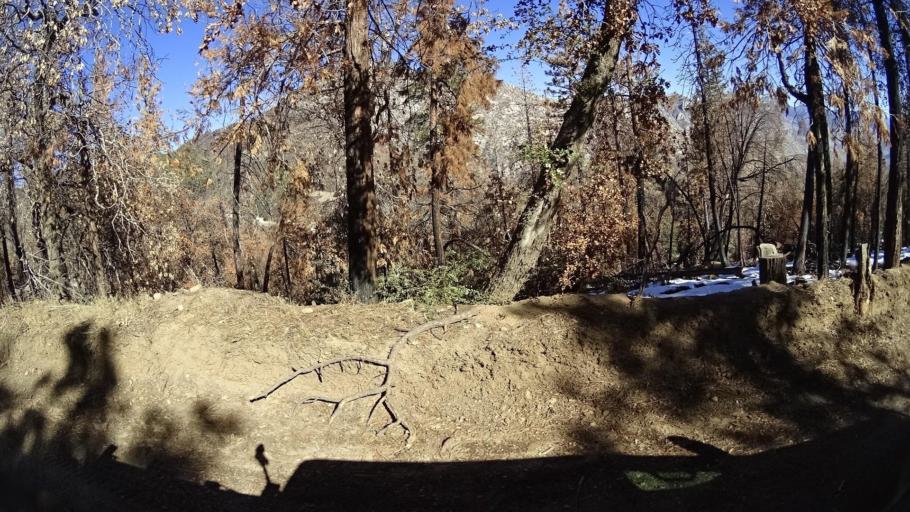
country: US
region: California
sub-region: Kern County
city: Alta Sierra
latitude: 35.7169
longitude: -118.5322
